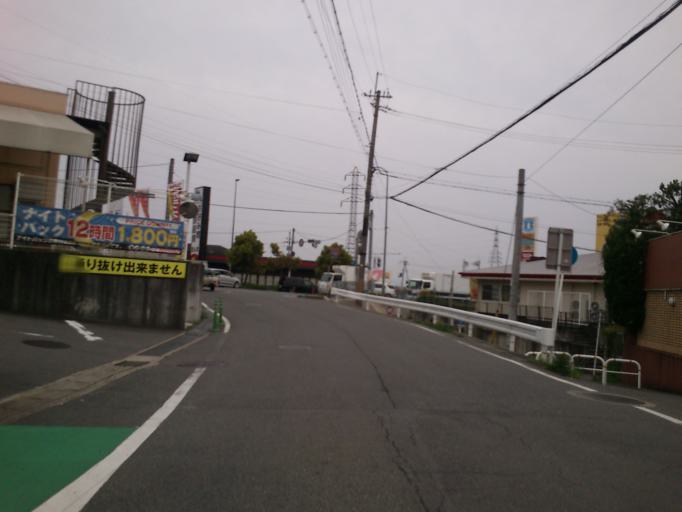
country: JP
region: Kyoto
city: Yawata
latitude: 34.8550
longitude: 135.7085
